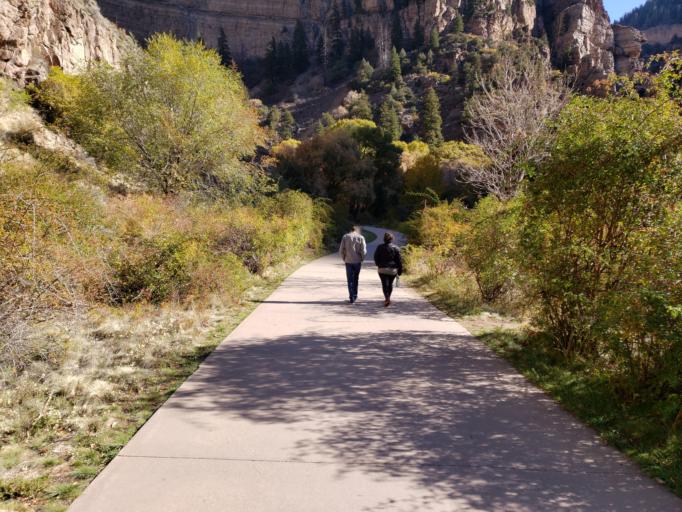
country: US
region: Colorado
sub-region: Garfield County
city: Glenwood Springs
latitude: 39.5922
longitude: -107.1854
